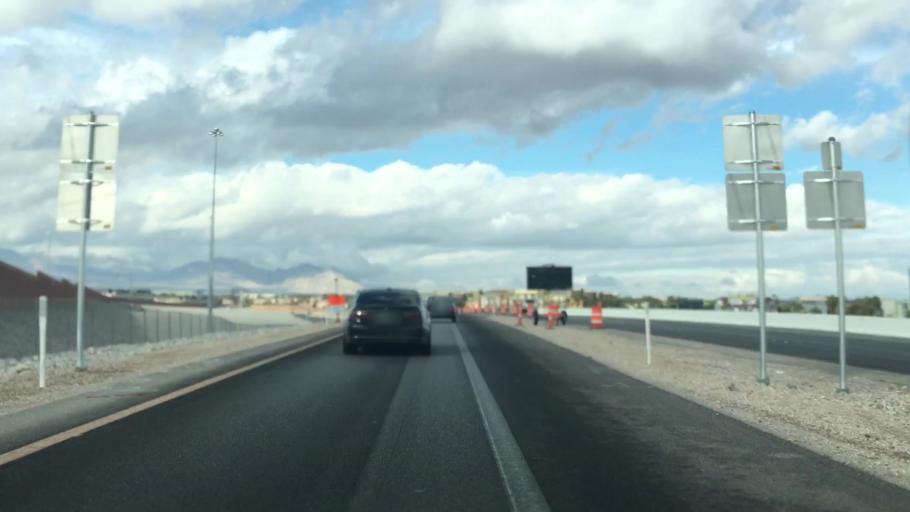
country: US
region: Nevada
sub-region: Clark County
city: Summerlin South
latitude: 36.0964
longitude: -115.2900
